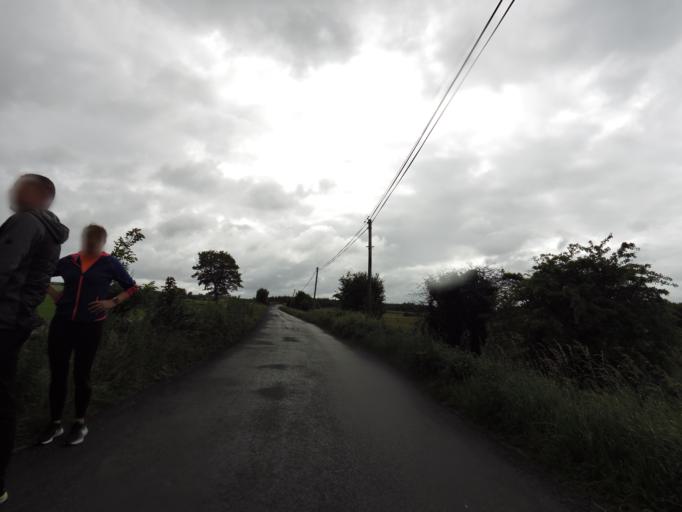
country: IE
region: Connaught
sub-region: County Galway
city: Athenry
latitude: 53.2901
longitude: -8.6972
